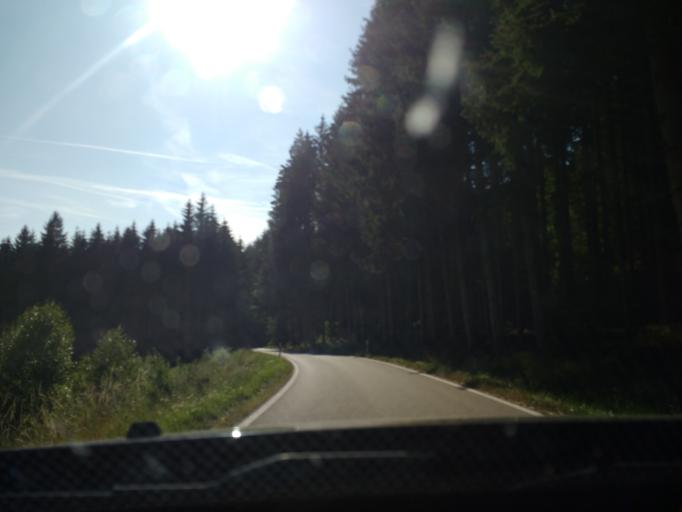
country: DE
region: Rheinland-Pfalz
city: Densborn
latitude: 50.1274
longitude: 6.6245
